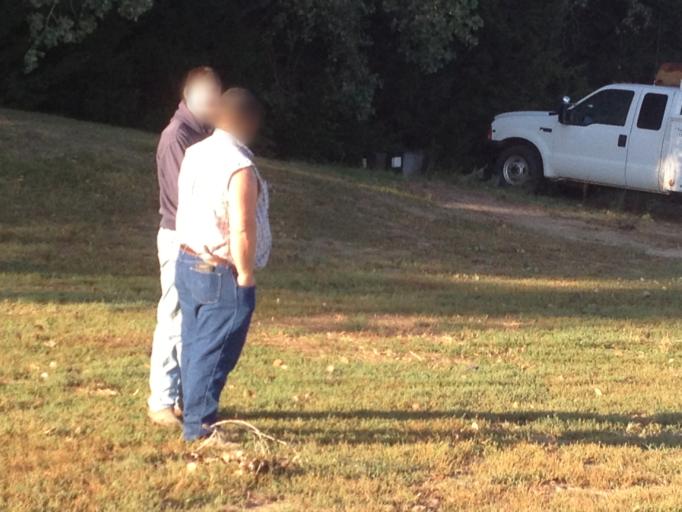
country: US
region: Kansas
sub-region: Barton County
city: Ellinwood
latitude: 38.2957
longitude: -98.6657
